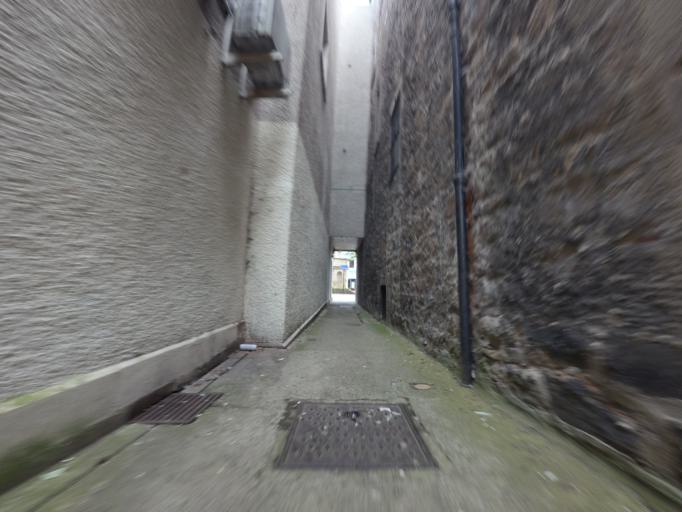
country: GB
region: Scotland
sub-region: Moray
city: Elgin
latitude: 57.6484
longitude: -3.3145
